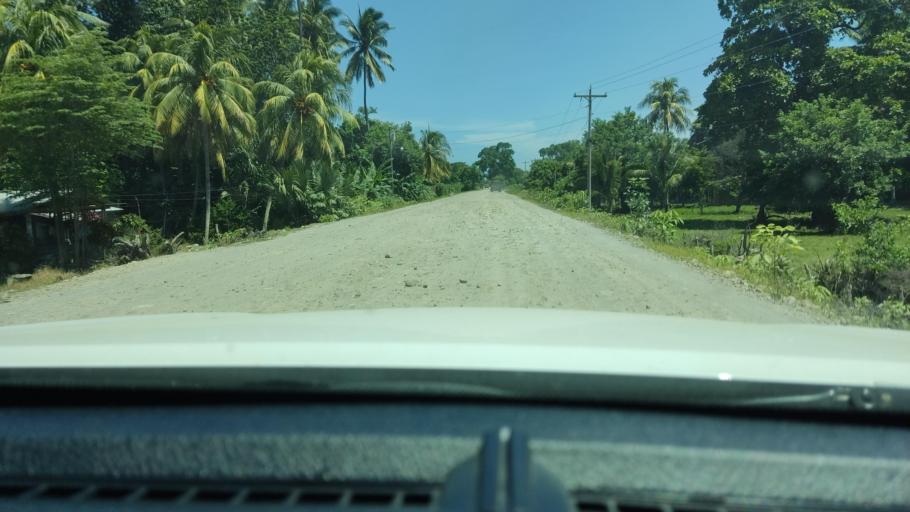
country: SV
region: Ahuachapan
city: San Francisco Menendez
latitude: 13.7911
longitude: -90.1176
